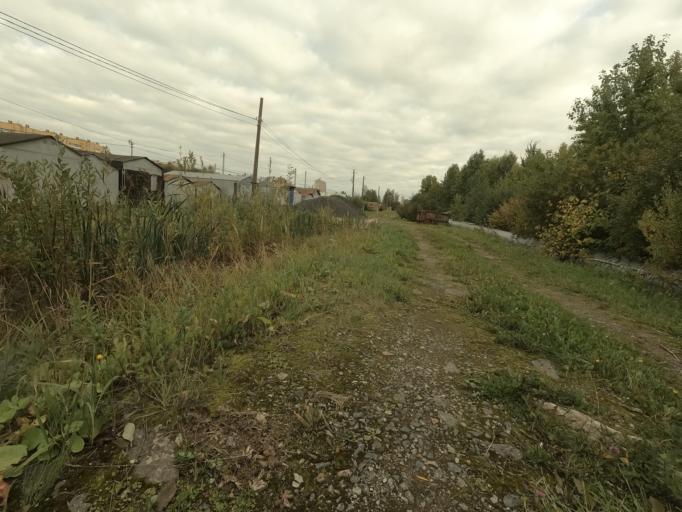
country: RU
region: Leningrad
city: Rybatskoye
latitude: 59.8364
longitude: 30.4892
